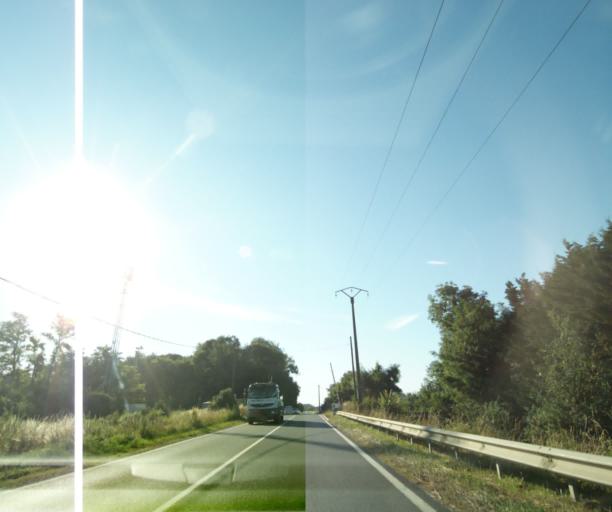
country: FR
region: Ile-de-France
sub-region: Departement de Seine-et-Marne
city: Cannes-Ecluse
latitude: 48.3813
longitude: 2.9768
